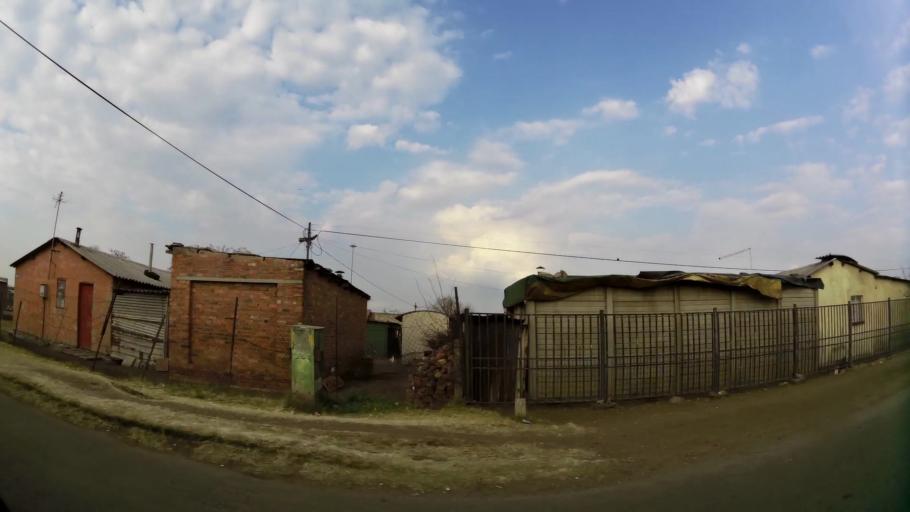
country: ZA
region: Gauteng
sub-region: Sedibeng District Municipality
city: Vanderbijlpark
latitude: -26.6894
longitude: 27.8802
